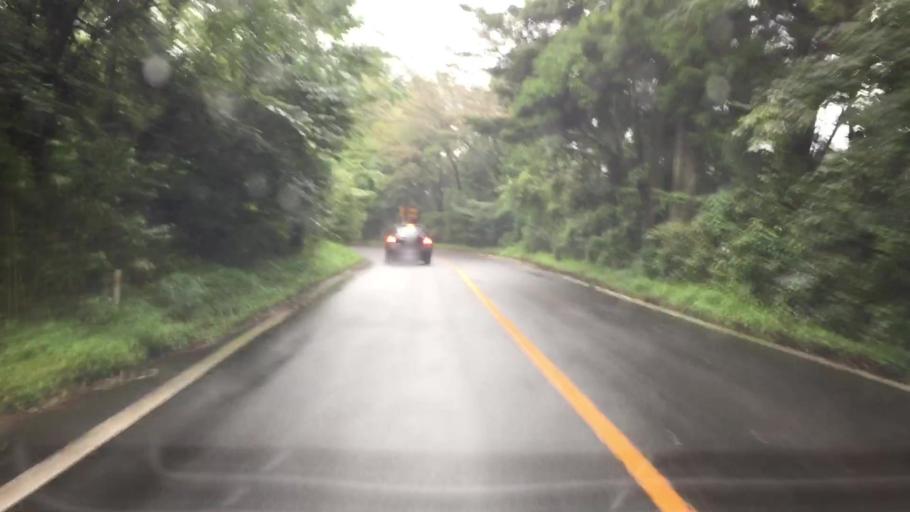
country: JP
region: Yamanashi
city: Fujikawaguchiko
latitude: 35.3959
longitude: 138.6099
